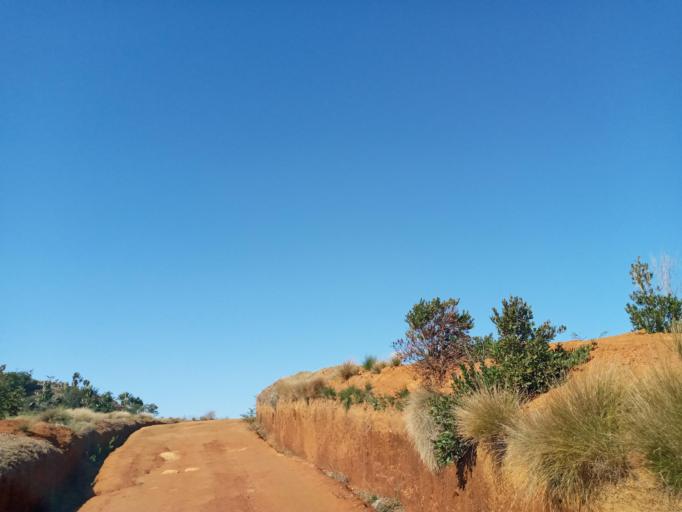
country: MG
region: Anosy
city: Fort Dauphin
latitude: -24.9121
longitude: 47.0807
